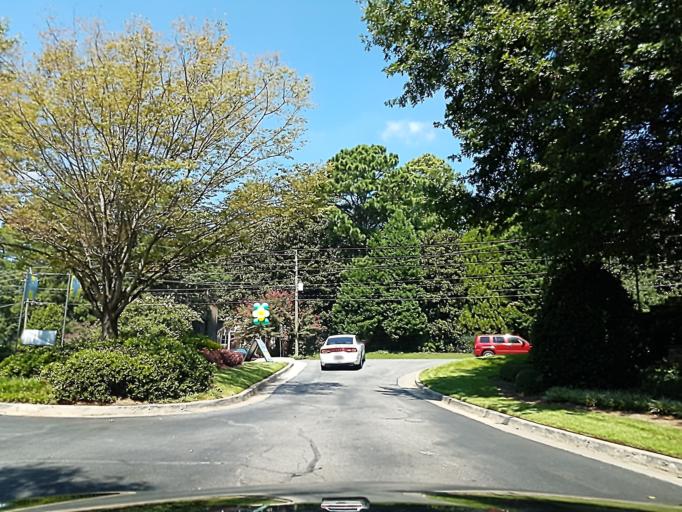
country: US
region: Georgia
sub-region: DeKalb County
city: North Druid Hills
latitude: 33.8155
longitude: -84.3167
